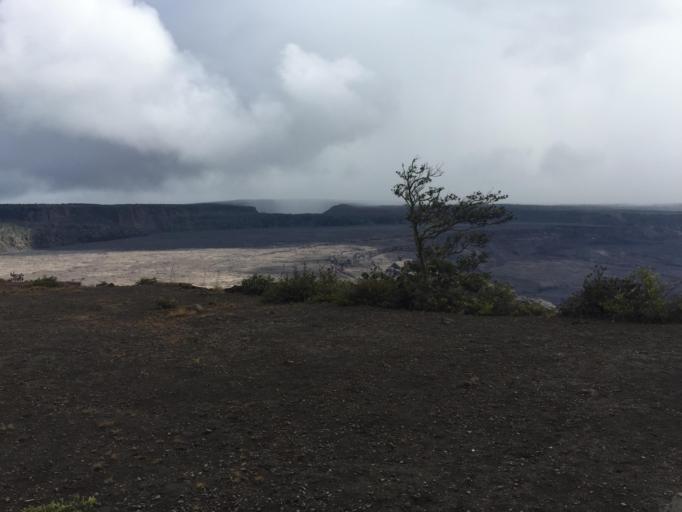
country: US
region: Hawaii
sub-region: Hawaii County
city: Volcano
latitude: 19.4227
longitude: -155.2848
